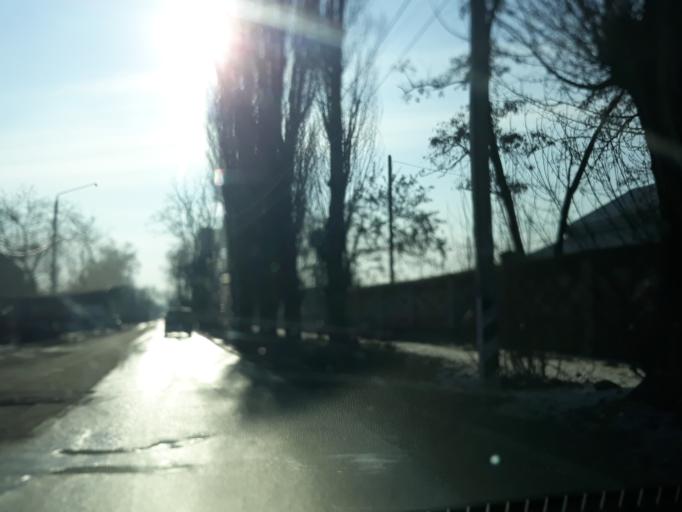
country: RU
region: Rostov
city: Taganrog
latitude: 47.2252
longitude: 38.9099
